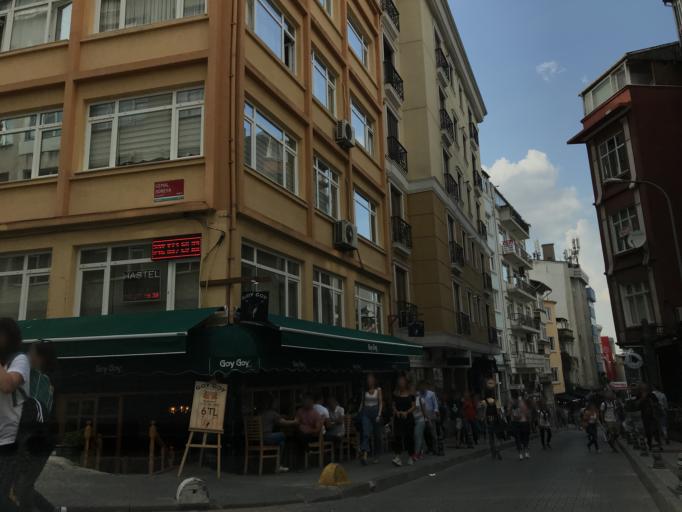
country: TR
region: Istanbul
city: UEskuedar
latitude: 40.9878
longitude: 29.0244
